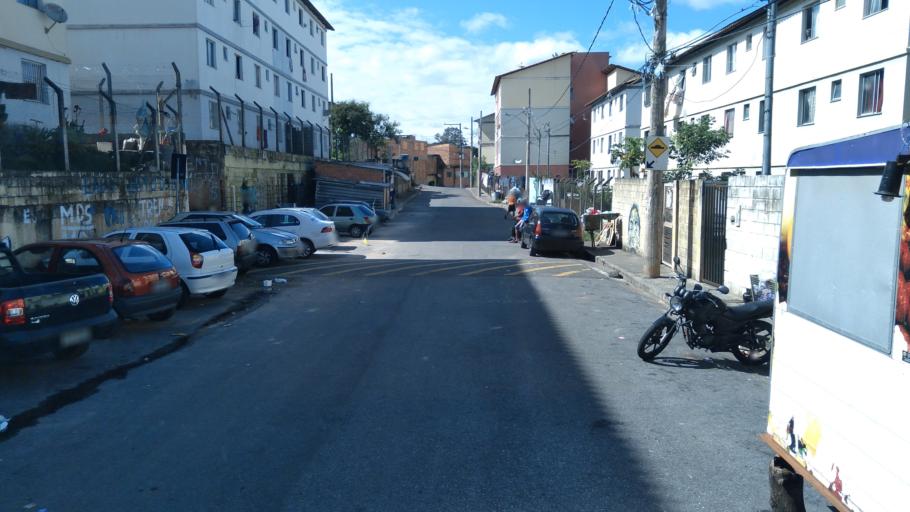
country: BR
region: Minas Gerais
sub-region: Belo Horizonte
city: Belo Horizonte
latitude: -19.9019
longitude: -43.9513
